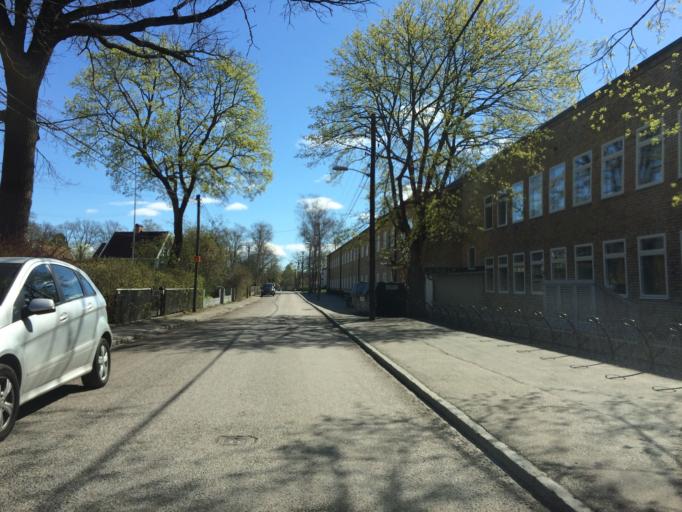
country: SE
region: Stockholm
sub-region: Huddinge Kommun
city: Huddinge
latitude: 59.2782
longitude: 17.9820
